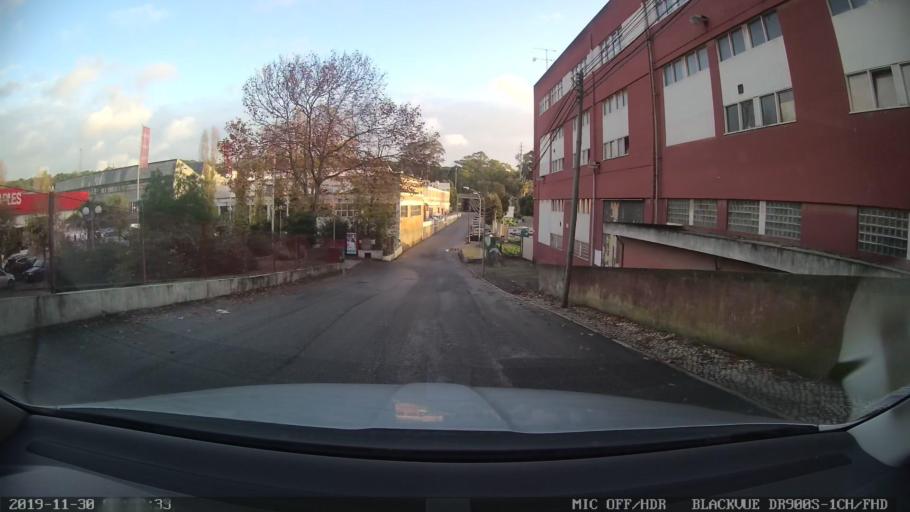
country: PT
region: Lisbon
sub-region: Oeiras
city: Alges
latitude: 38.7217
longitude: -9.2166
